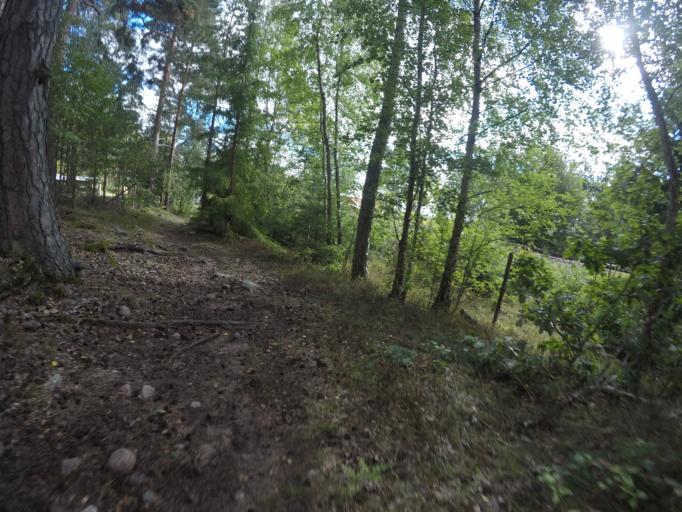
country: SE
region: Soedermanland
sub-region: Eskilstuna Kommun
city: Kvicksund
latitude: 59.4978
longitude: 16.2719
